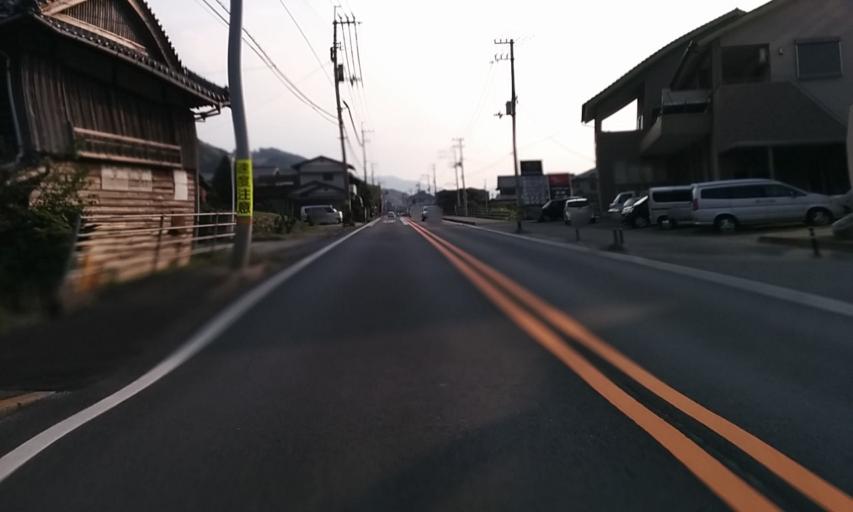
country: JP
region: Ehime
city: Saijo
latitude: 33.8844
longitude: 133.0813
